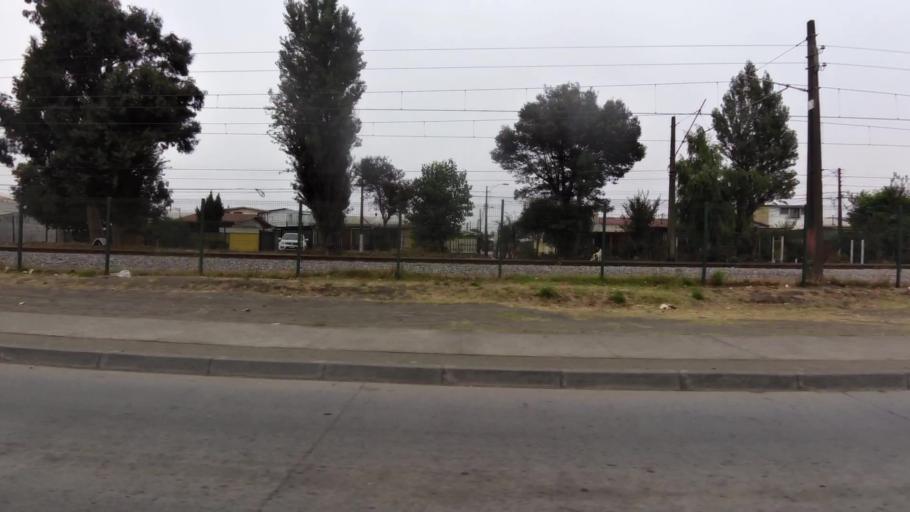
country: CL
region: Biobio
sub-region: Provincia de Concepcion
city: Concepcion
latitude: -36.7983
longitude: -73.0807
